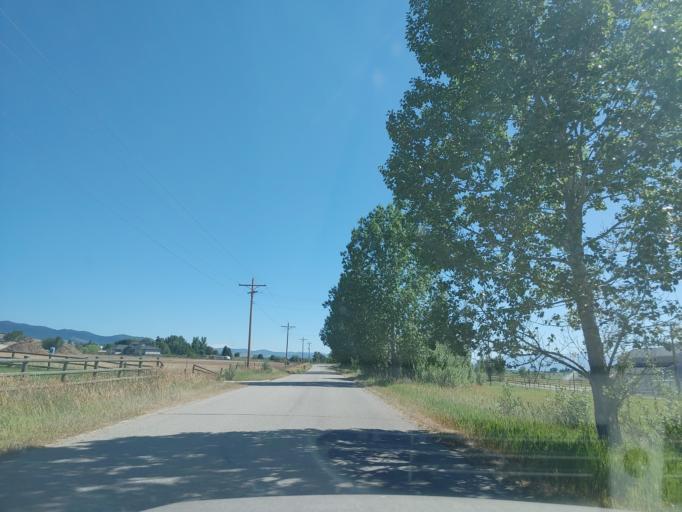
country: US
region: Montana
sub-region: Ravalli County
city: Hamilton
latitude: 46.3478
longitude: -114.0616
